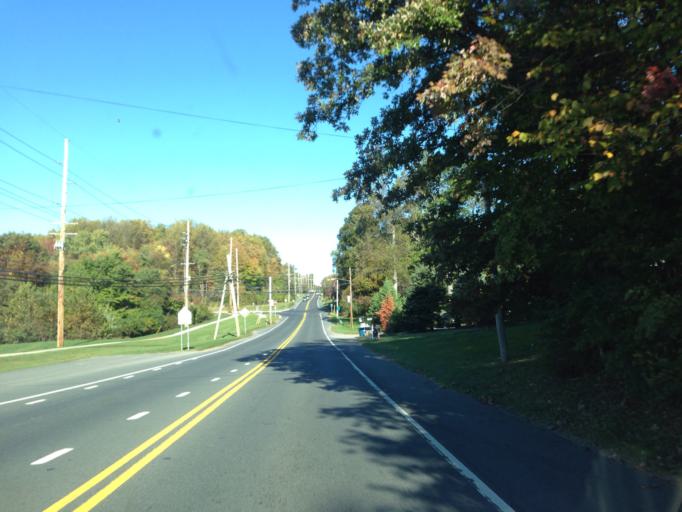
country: US
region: Maryland
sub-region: Montgomery County
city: Clarksburg
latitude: 39.2290
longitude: -77.2670
